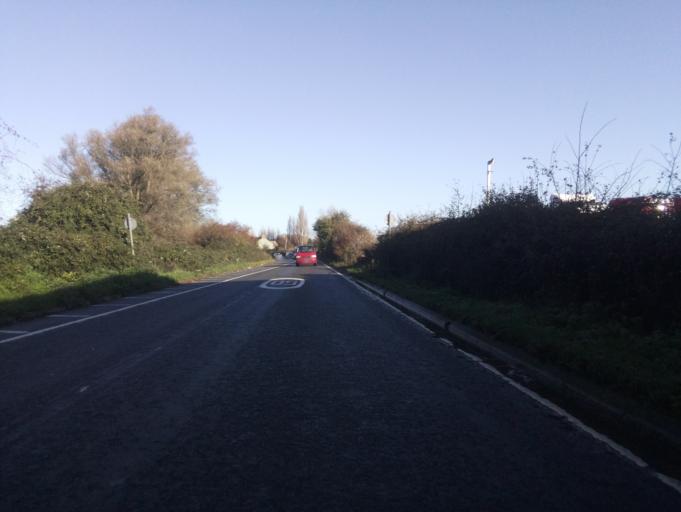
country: GB
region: England
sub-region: Somerset
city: Puriton
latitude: 51.1596
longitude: -2.9861
